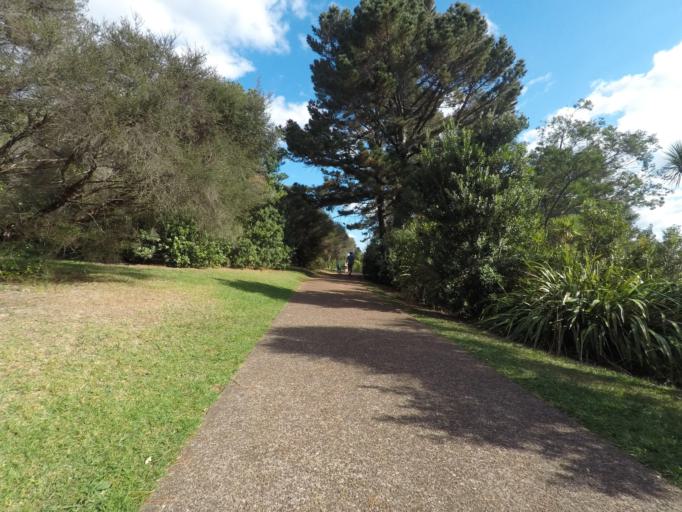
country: NZ
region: Auckland
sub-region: Auckland
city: Rosebank
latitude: -36.8846
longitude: 174.6955
